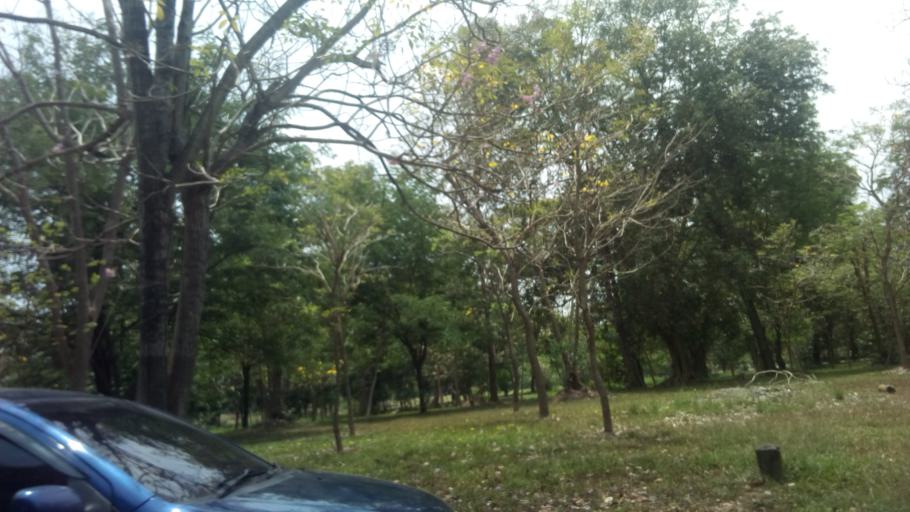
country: TH
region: Bangkok
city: Thawi Watthana
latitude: 13.7726
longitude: 100.3154
